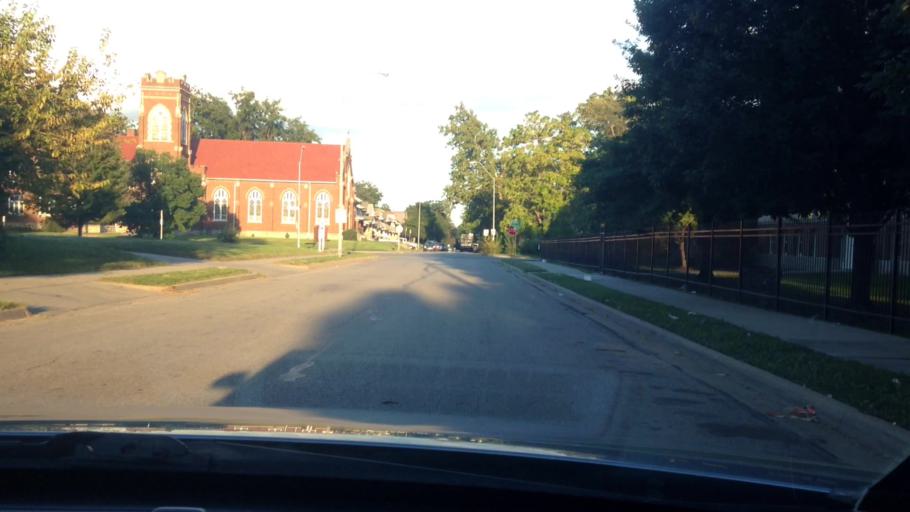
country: US
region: Missouri
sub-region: Jackson County
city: Kansas City
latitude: 39.0716
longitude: -94.5503
